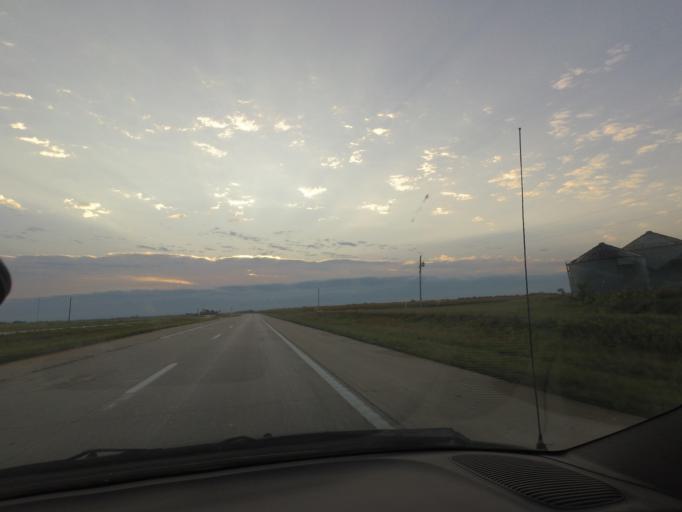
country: US
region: Missouri
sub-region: Macon County
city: Macon
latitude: 39.7499
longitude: -92.3009
